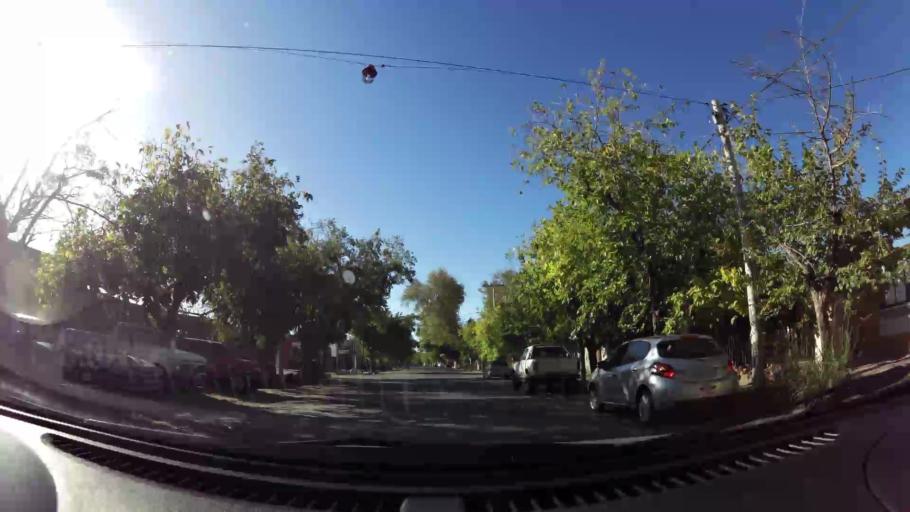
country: AR
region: San Juan
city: Villa Krause
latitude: -31.5684
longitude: -68.5200
